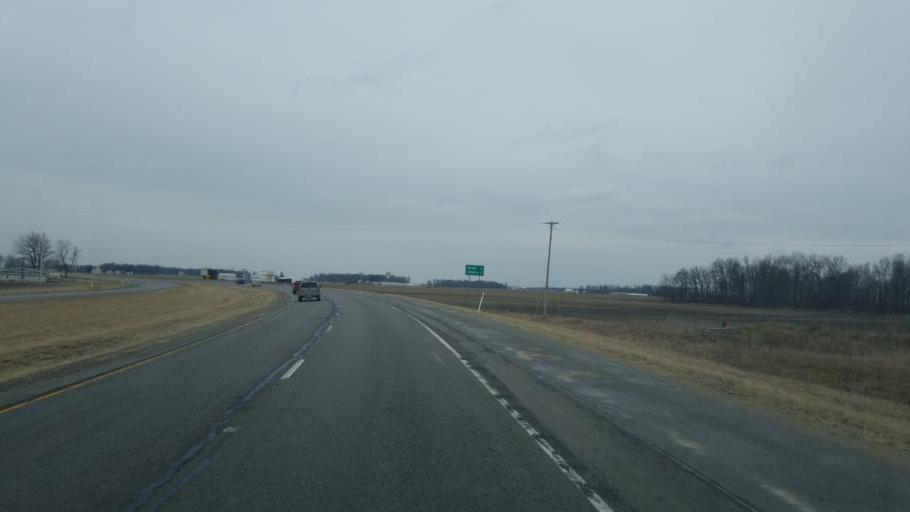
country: US
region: Indiana
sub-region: Adams County
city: Berne
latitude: 40.7439
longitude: -84.9555
